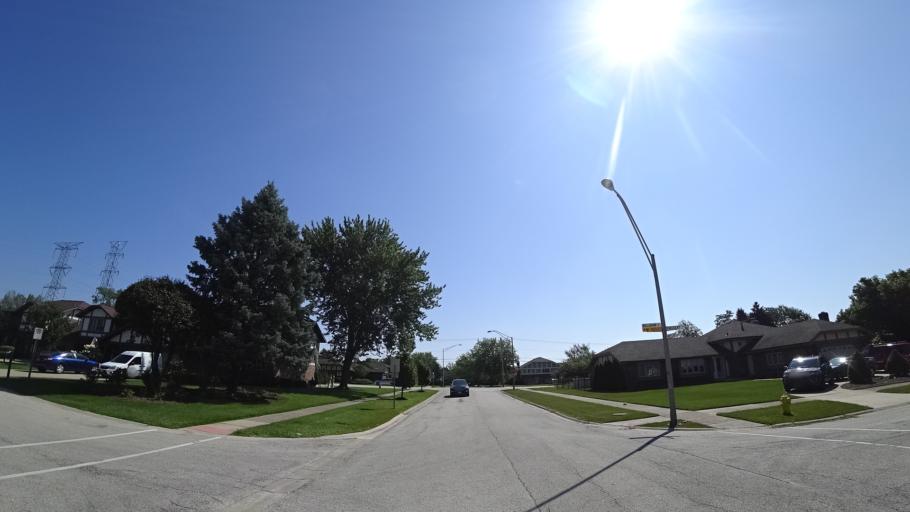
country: US
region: Illinois
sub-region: Cook County
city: Palos Park
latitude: 41.6369
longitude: -87.8206
